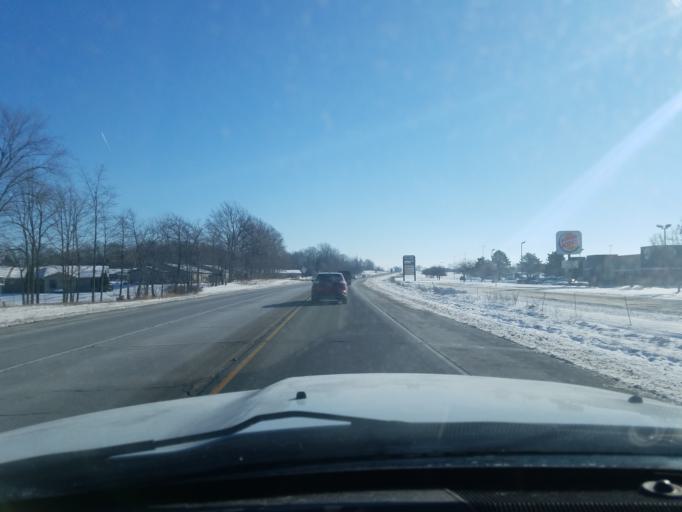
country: US
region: Indiana
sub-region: Noble County
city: Kendallville
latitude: 41.4514
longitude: -85.2468
